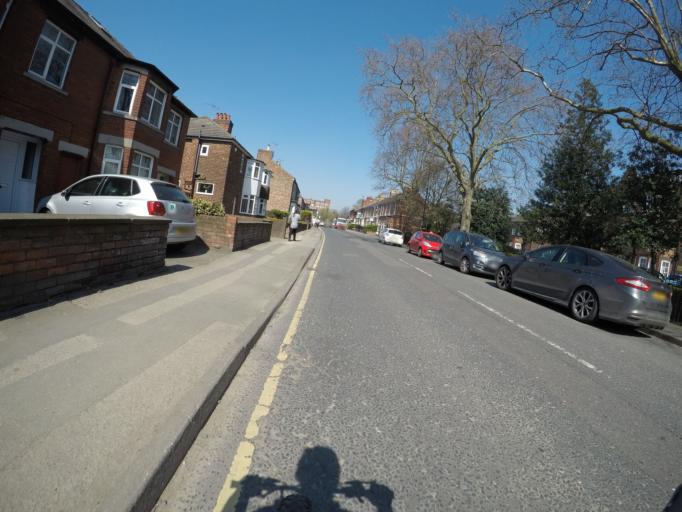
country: GB
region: England
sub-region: City of York
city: York
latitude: 53.9705
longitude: -1.0780
